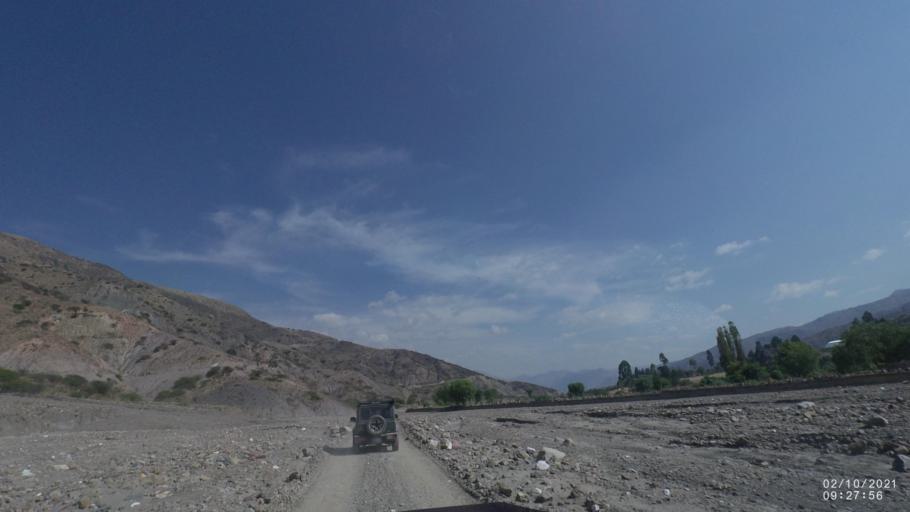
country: BO
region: Cochabamba
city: Irpa Irpa
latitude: -17.8542
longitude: -66.3171
